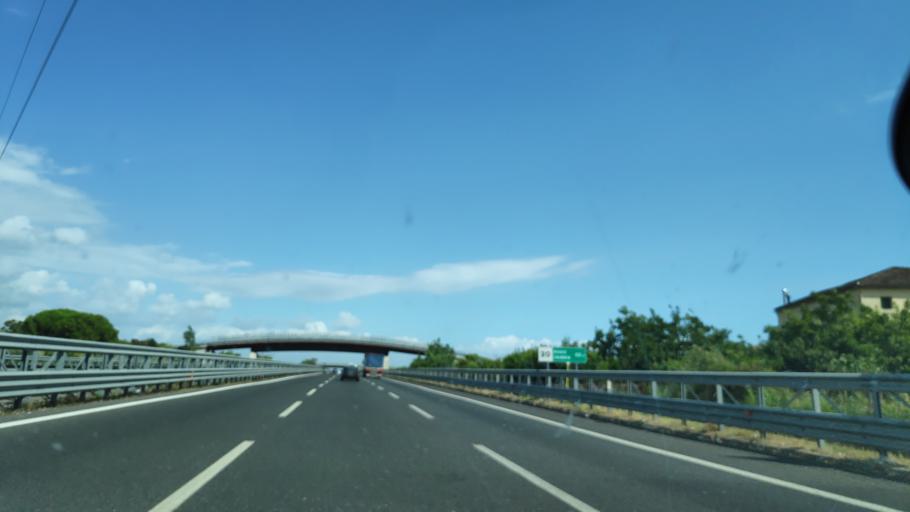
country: IT
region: Campania
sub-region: Provincia di Salerno
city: Pontecagnano
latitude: 40.6491
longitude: 14.8813
